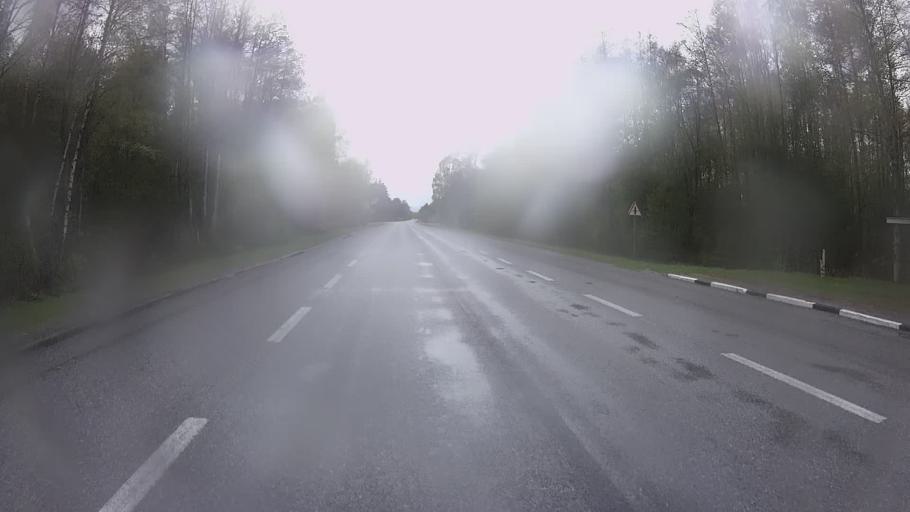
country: EE
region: Hiiumaa
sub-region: Kaerdla linn
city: Kardla
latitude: 58.8141
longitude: 22.7349
